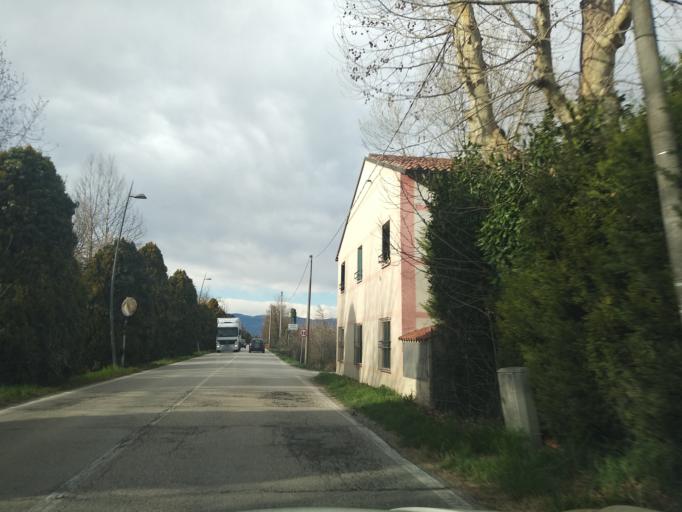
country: IT
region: Veneto
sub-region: Provincia di Vicenza
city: Bolzano Vicentino
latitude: 45.5935
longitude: 11.6231
